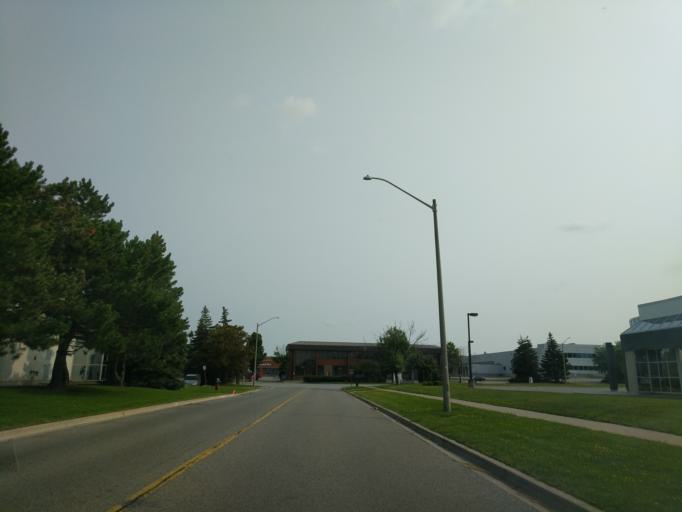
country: CA
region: Ontario
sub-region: York
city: Richmond Hill
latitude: 43.8572
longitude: -79.3881
